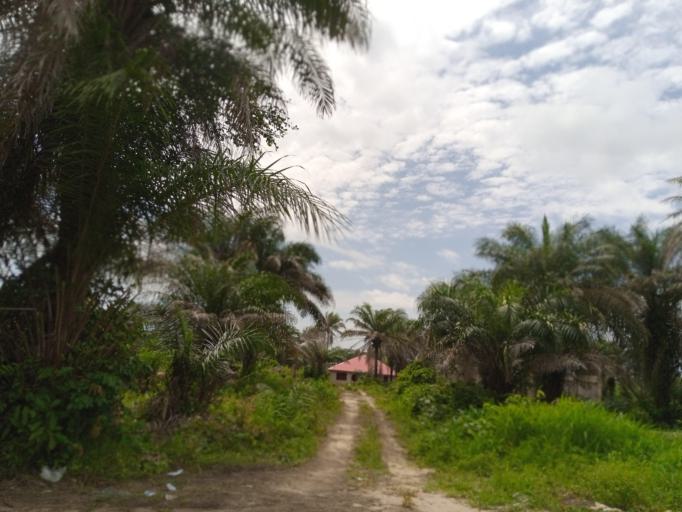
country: SL
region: Northern Province
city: Masoyila
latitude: 8.5560
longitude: -13.1612
